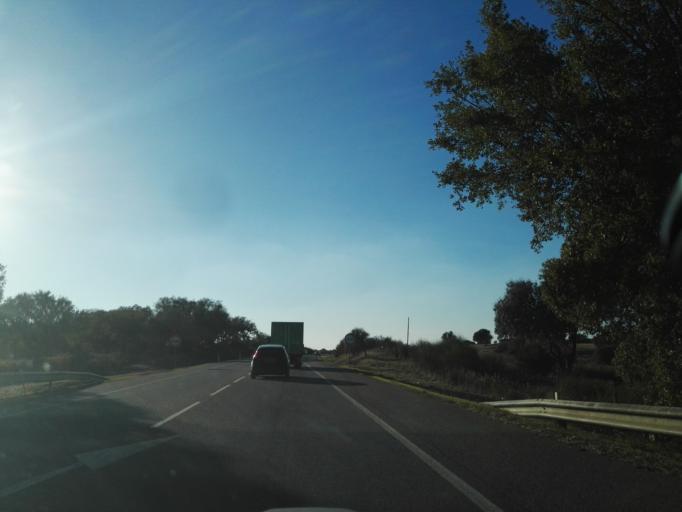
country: PT
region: Evora
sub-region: Borba
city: Borba
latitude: 38.8243
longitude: -7.5130
